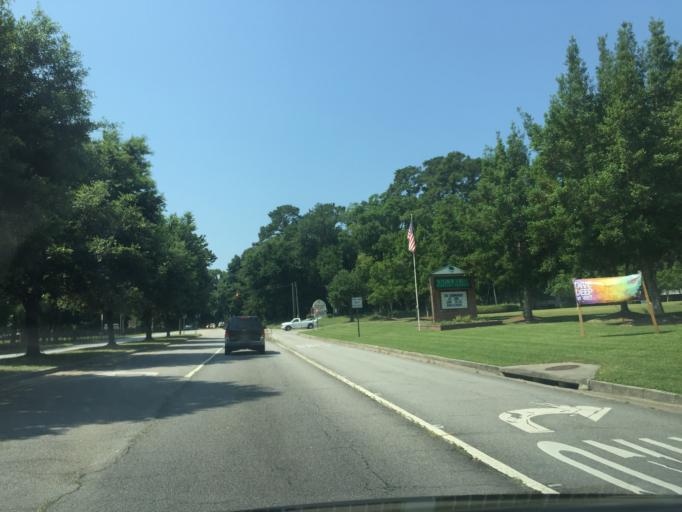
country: US
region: Georgia
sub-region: Chatham County
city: Montgomery
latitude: 31.9716
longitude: -81.1335
